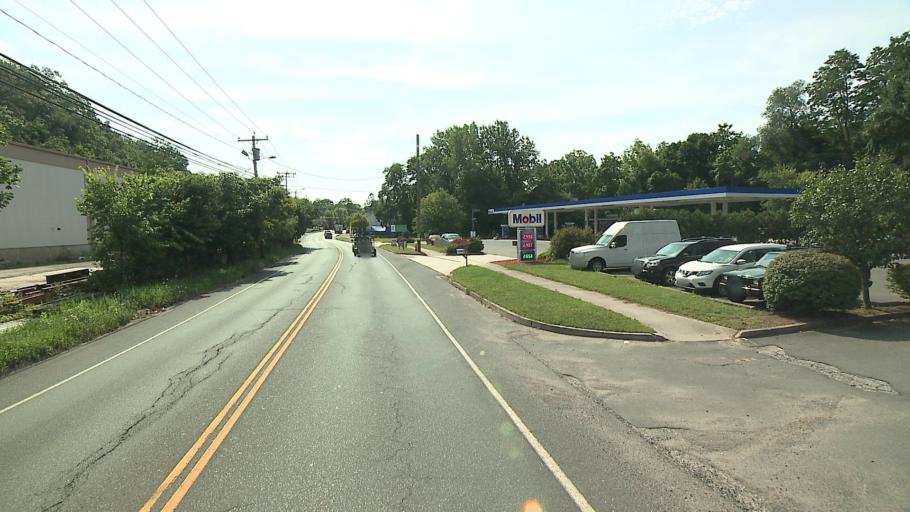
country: US
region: Connecticut
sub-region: Fairfield County
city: Danbury
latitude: 41.4187
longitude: -73.4654
